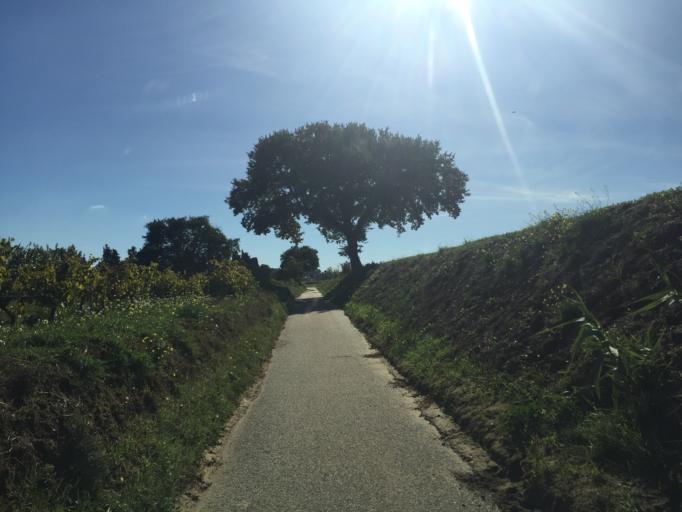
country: FR
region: Provence-Alpes-Cote d'Azur
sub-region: Departement du Vaucluse
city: Courthezon
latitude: 44.0892
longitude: 4.8526
